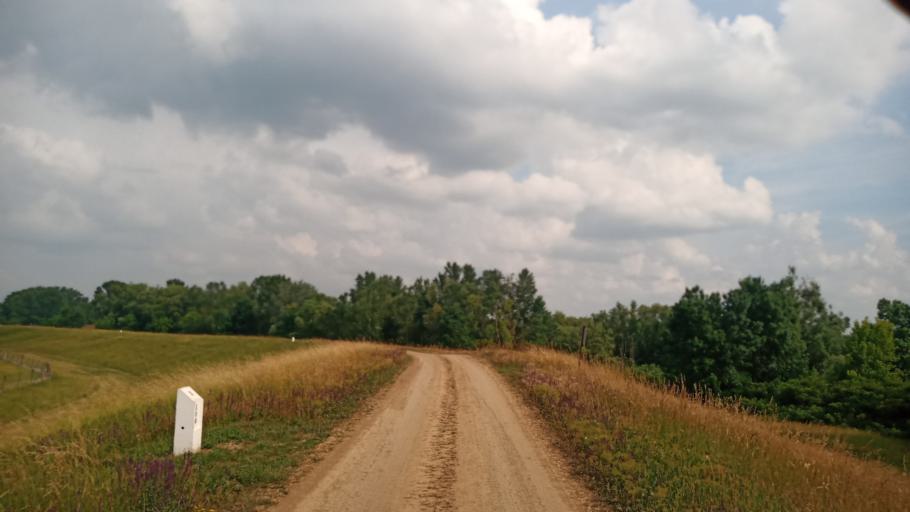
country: HU
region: Bekes
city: Gyula
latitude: 46.7051
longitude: 21.3058
